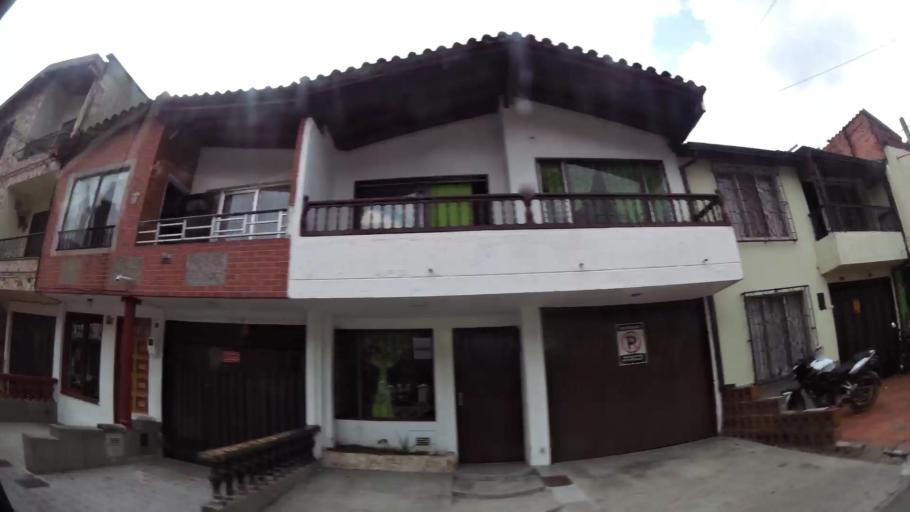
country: CO
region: Antioquia
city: Envigado
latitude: 6.1590
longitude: -75.5933
